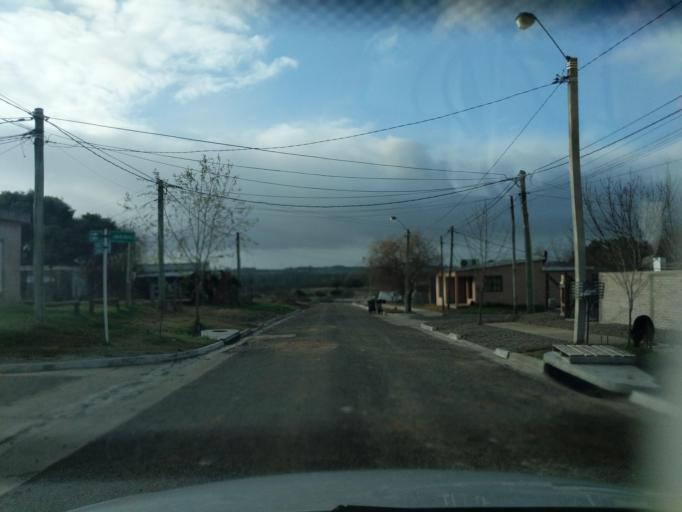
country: UY
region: Florida
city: Florida
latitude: -34.0840
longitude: -56.2106
